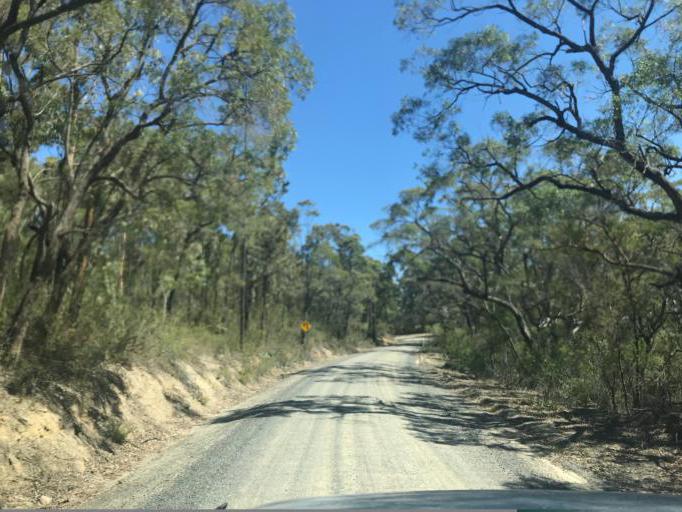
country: AU
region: New South Wales
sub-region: Wyong Shire
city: Little Jilliby
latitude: -33.1483
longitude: 151.0810
